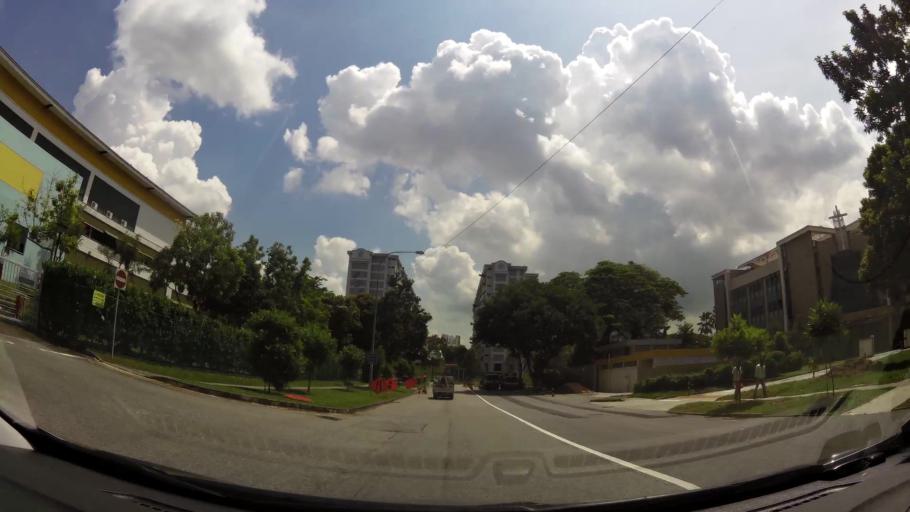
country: SG
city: Singapore
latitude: 1.3678
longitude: 103.8352
